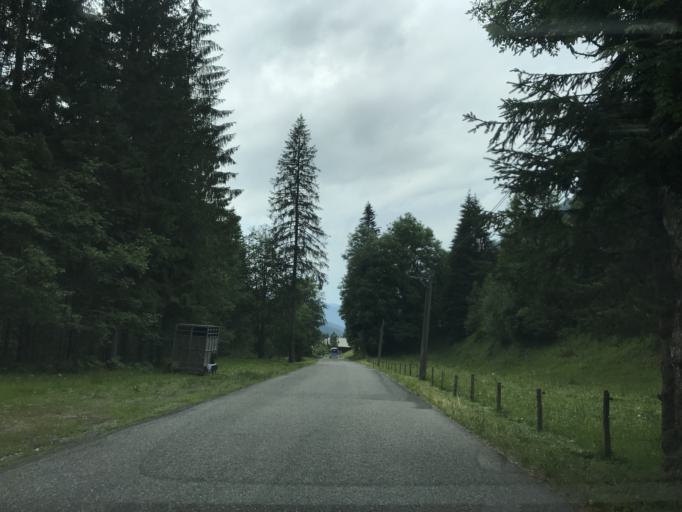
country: FR
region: Rhone-Alpes
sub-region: Departement de la Haute-Savoie
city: Morzine
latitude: 46.1526
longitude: 6.7399
